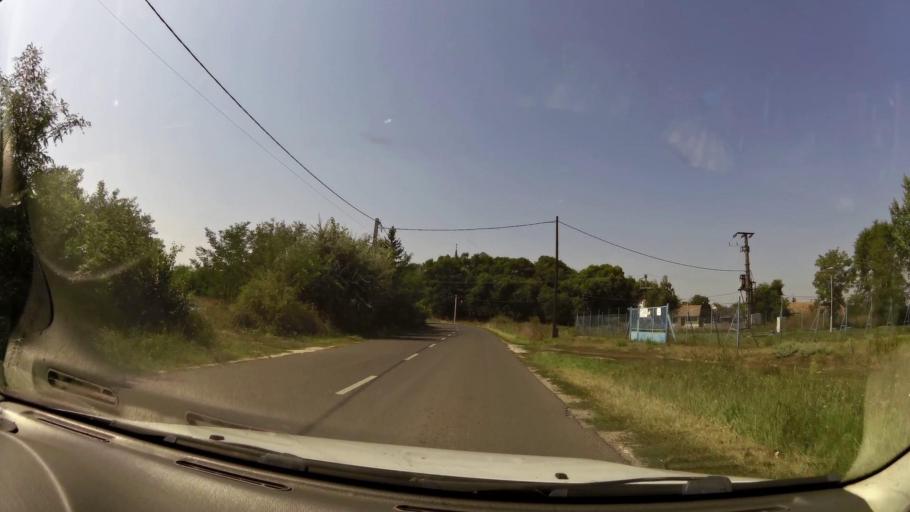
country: HU
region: Pest
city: Tapioszentmarton
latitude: 47.3475
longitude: 19.7503
